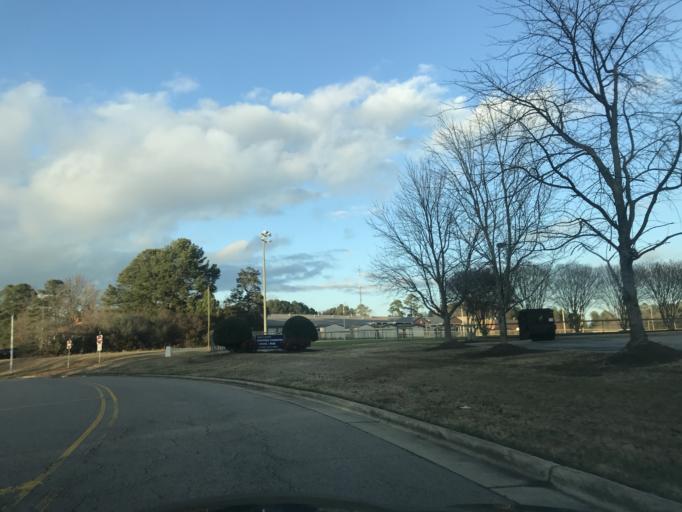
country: US
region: North Carolina
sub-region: Wake County
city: Rolesville
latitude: 35.9168
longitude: -78.4635
